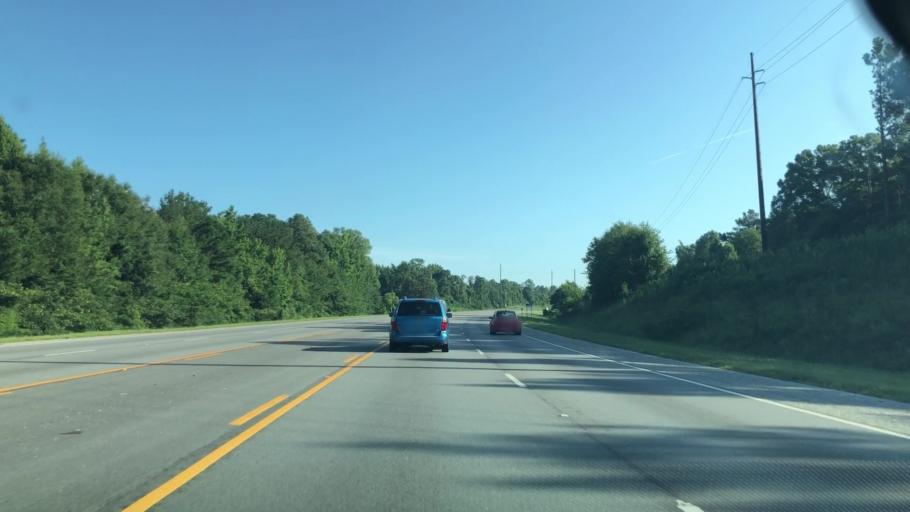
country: US
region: Alabama
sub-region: Calhoun County
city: Bynum
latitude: 33.6096
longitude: -85.9287
